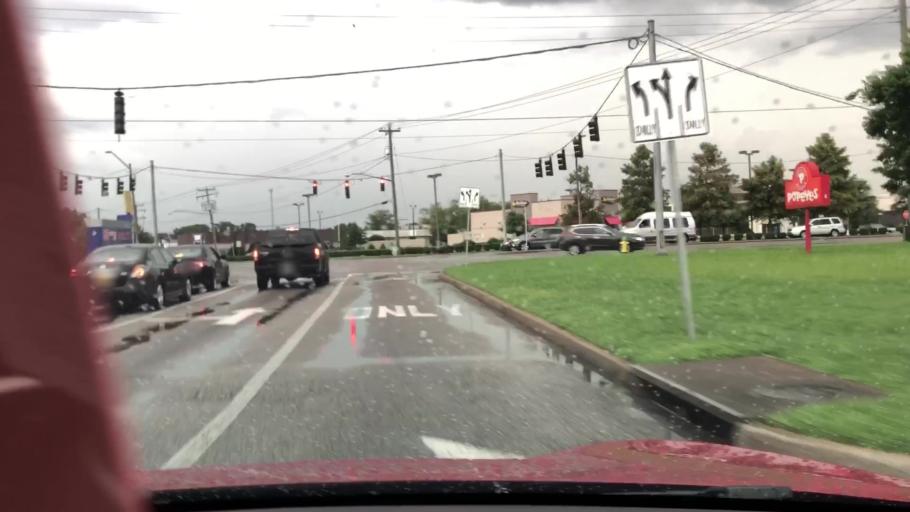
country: US
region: Virginia
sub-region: City of Chesapeake
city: Chesapeake
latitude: 36.8562
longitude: -76.2035
